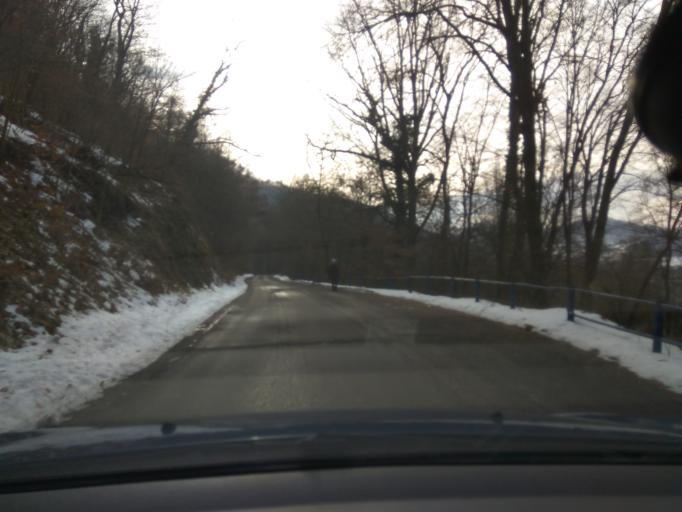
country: SK
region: Banskobystricky
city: Zarnovica
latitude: 48.4770
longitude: 18.7347
